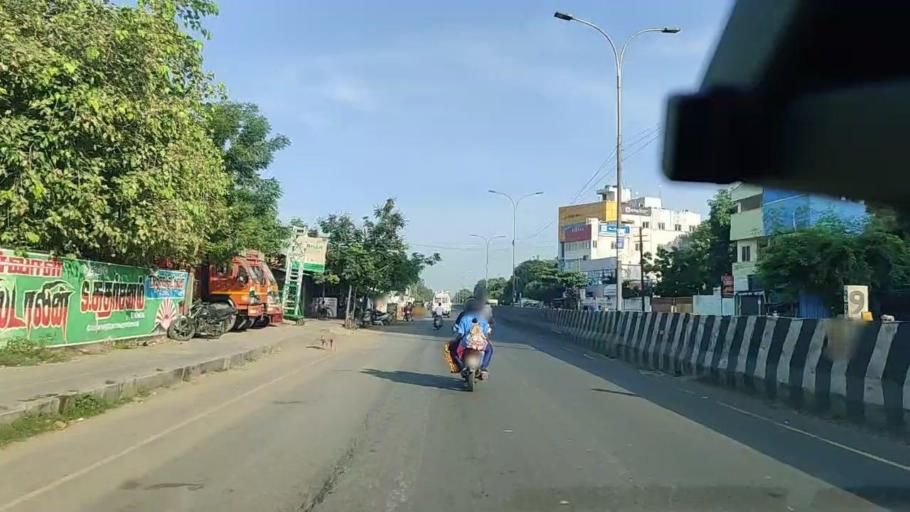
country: IN
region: Tamil Nadu
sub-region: Thiruvallur
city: Chinnasekkadu
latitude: 13.1360
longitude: 80.2317
